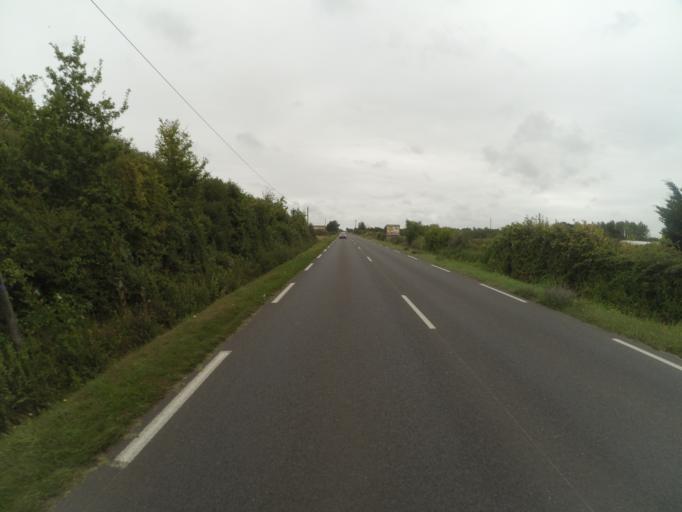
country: FR
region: Pays de la Loire
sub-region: Departement de la Vendee
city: Sallertaine
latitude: 46.8803
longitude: -1.9584
